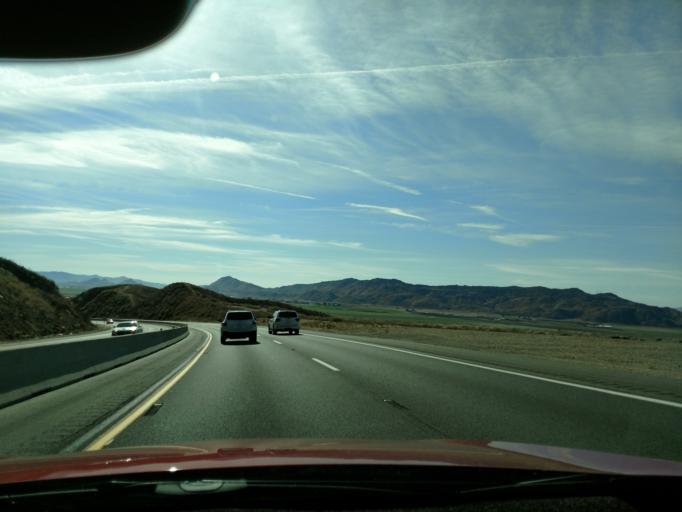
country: US
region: California
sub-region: Riverside County
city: Beaumont
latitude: 33.8600
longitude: -117.0091
